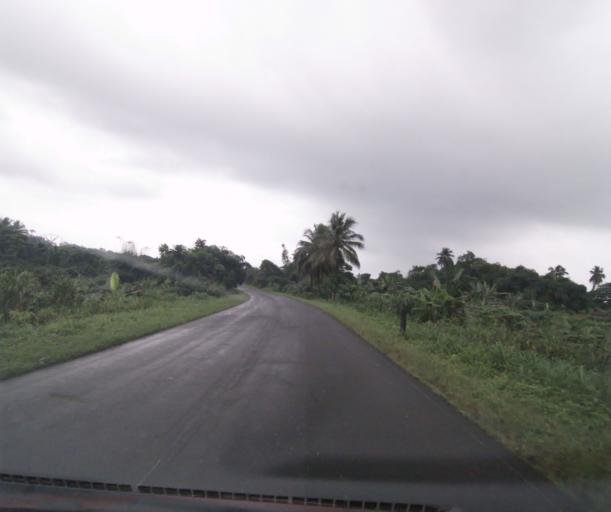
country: CM
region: South-West Province
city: Idenao
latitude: 4.1300
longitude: 8.9880
